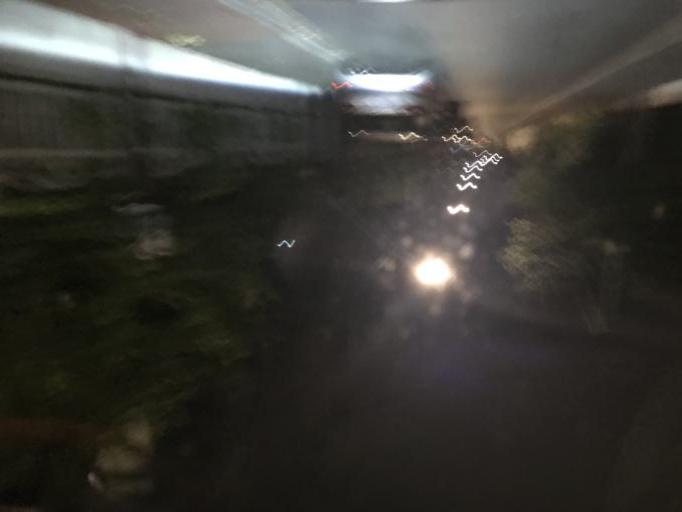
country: FR
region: Ile-de-France
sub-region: Departement du Val-d'Oise
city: Bezons
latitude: 48.9294
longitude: 2.2029
